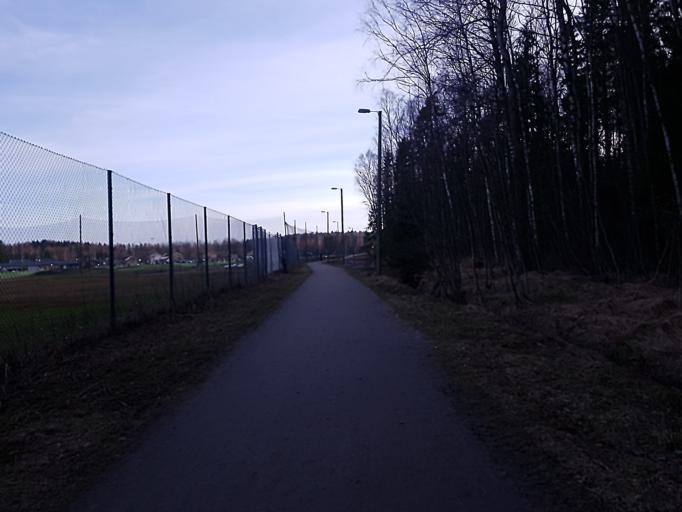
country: FI
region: Uusimaa
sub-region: Helsinki
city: Helsinki
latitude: 60.2593
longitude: 24.9336
